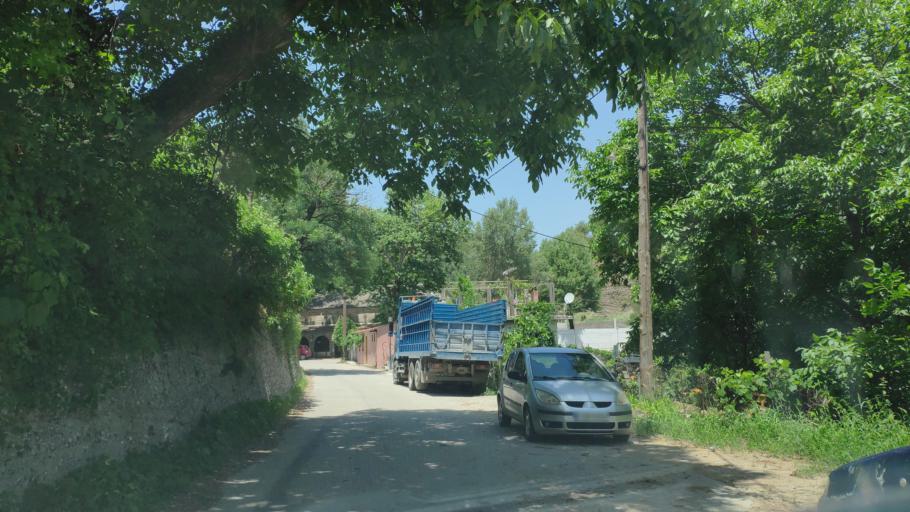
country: GR
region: Epirus
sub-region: Nomos Artas
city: Ano Kalentini
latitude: 39.2034
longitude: 21.3399
